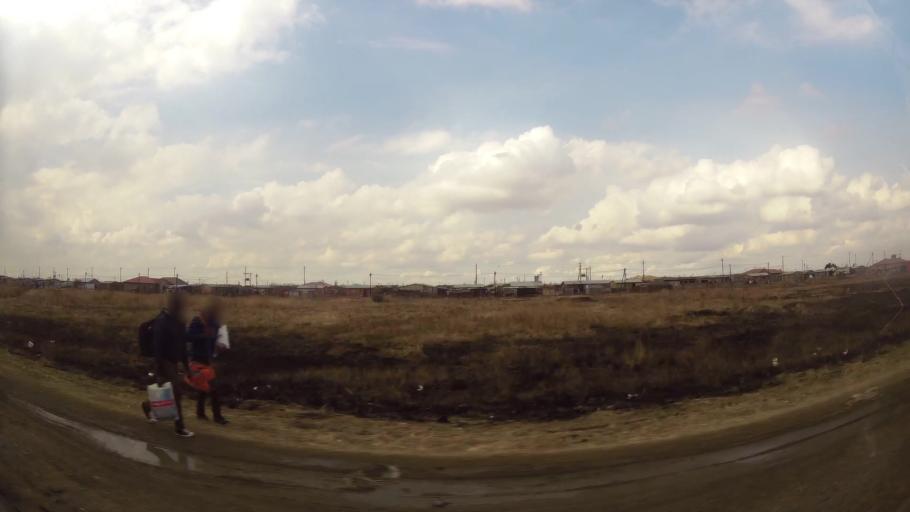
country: ZA
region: Orange Free State
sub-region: Fezile Dabi District Municipality
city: Sasolburg
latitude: -26.8550
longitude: 27.8887
